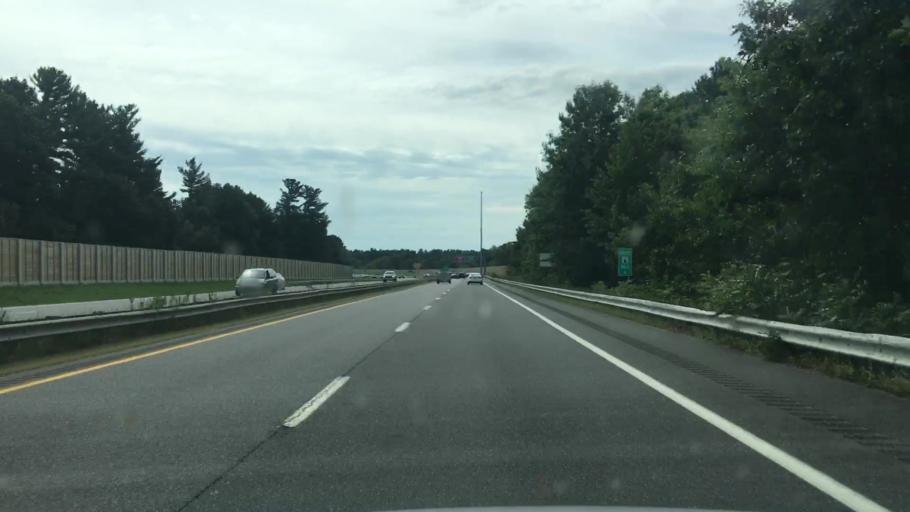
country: US
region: Maine
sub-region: York County
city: Eliot
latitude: 43.1442
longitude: -70.8433
